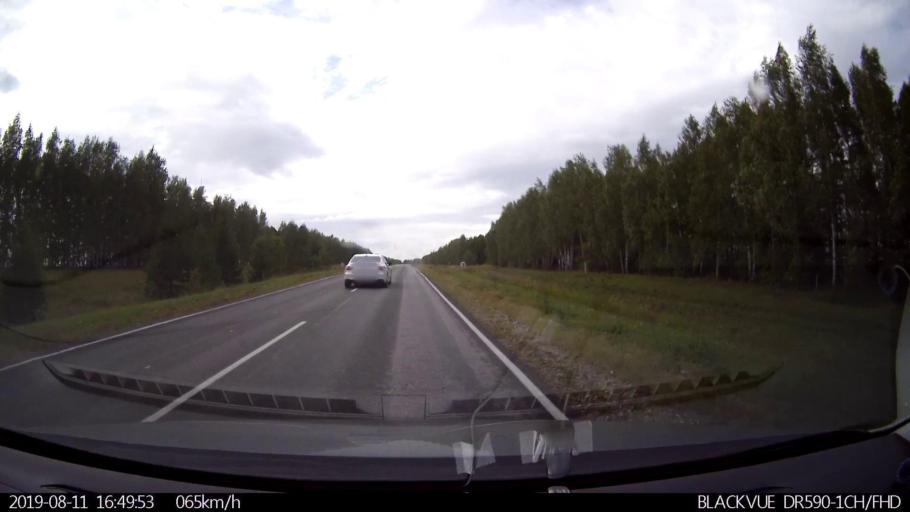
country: RU
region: Ulyanovsk
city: Mayna
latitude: 54.2242
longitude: 47.6935
